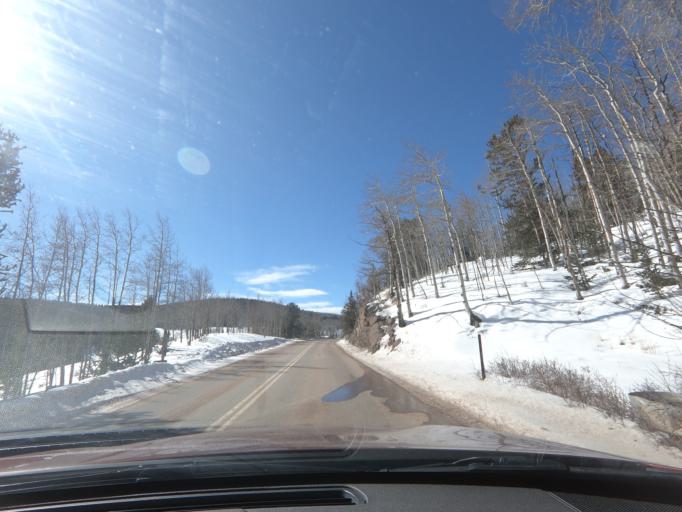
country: US
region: Colorado
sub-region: Teller County
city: Cripple Creek
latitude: 38.7428
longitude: -105.1073
